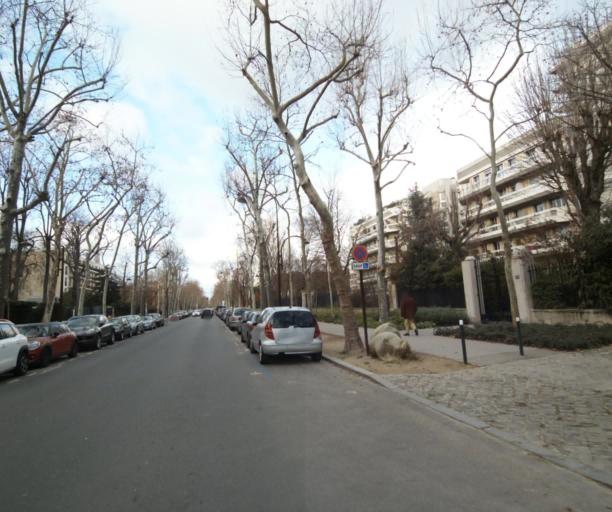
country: FR
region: Ile-de-France
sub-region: Departement des Hauts-de-Seine
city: Neuilly-sur-Seine
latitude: 48.8862
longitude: 2.2797
